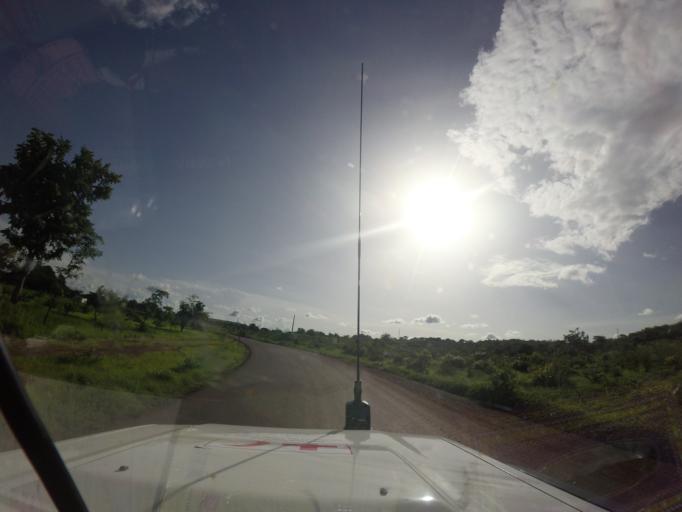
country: GN
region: Kindia
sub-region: Kindia
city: Kindia
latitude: 10.0832
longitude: -12.5853
